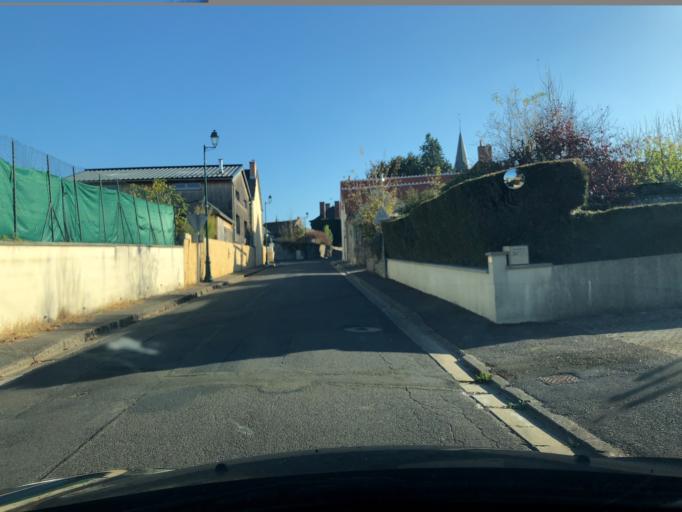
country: FR
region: Centre
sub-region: Departement d'Indre-et-Loire
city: Neuvy-le-Roi
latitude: 47.6054
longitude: 0.5934
